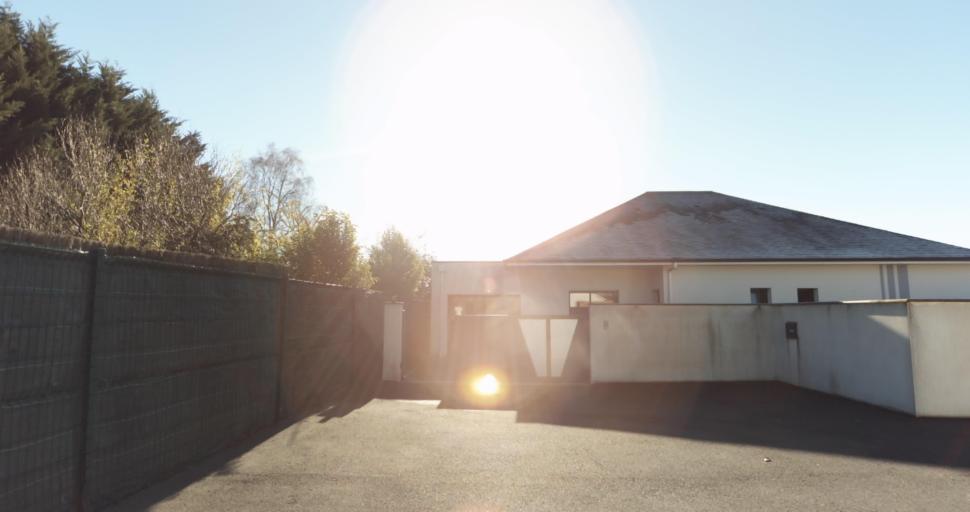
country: FR
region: Aquitaine
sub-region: Departement des Pyrenees-Atlantiques
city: Morlaas
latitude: 43.3432
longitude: -0.2574
